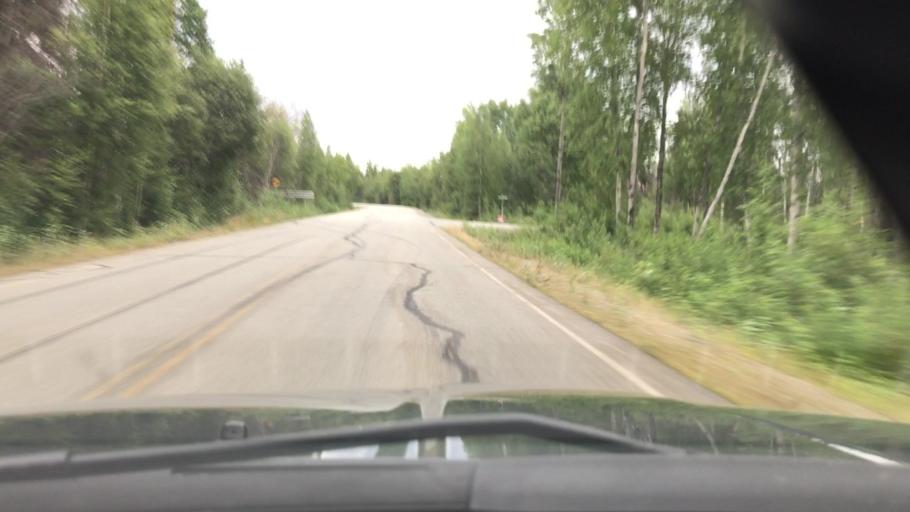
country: US
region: Alaska
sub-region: Matanuska-Susitna Borough
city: Willow
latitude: 61.7605
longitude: -150.1218
